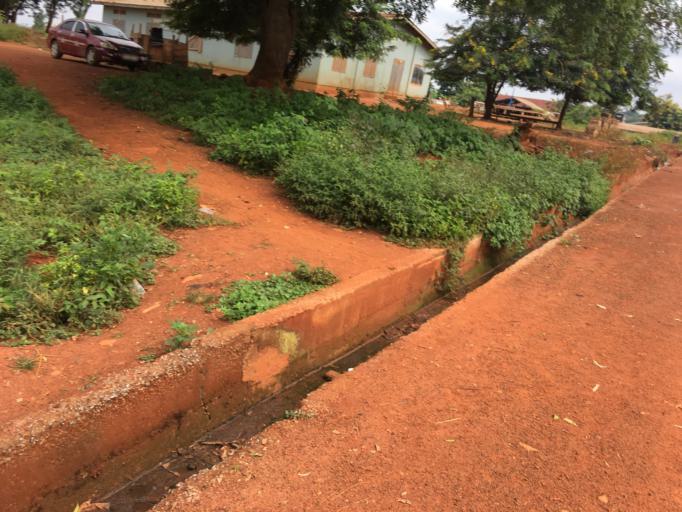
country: GH
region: Western
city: Bibiani
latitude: 6.8075
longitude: -2.5243
